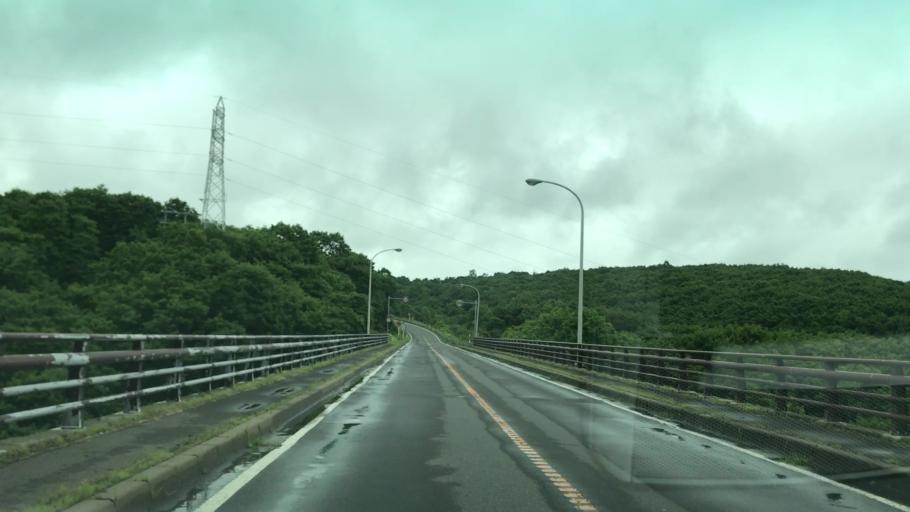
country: JP
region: Hokkaido
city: Muroran
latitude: 42.3810
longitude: 140.9678
